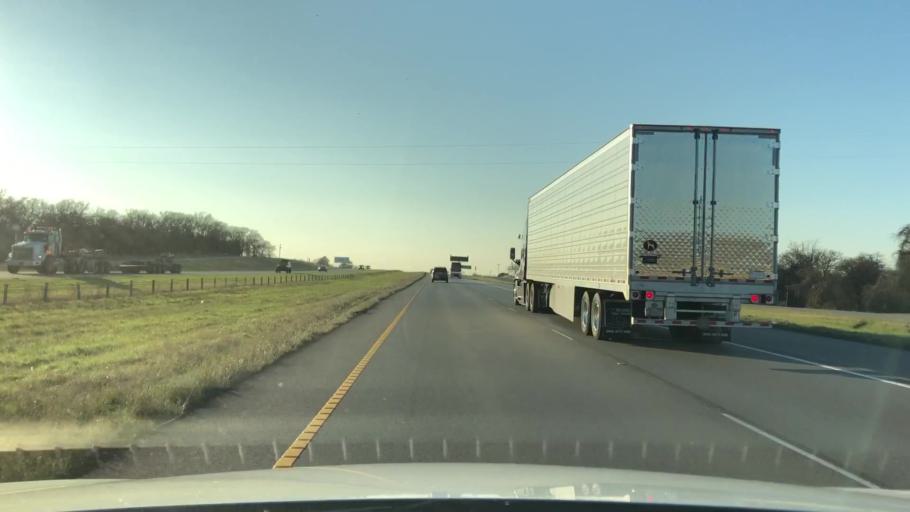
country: US
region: Texas
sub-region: Caldwell County
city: Luling
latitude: 29.6539
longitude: -97.5618
